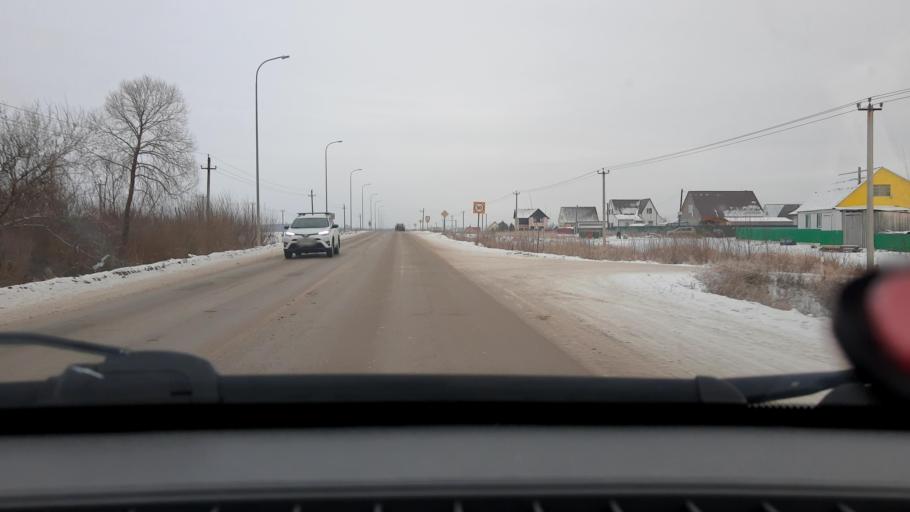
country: RU
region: Bashkortostan
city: Iglino
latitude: 54.8530
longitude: 56.4298
